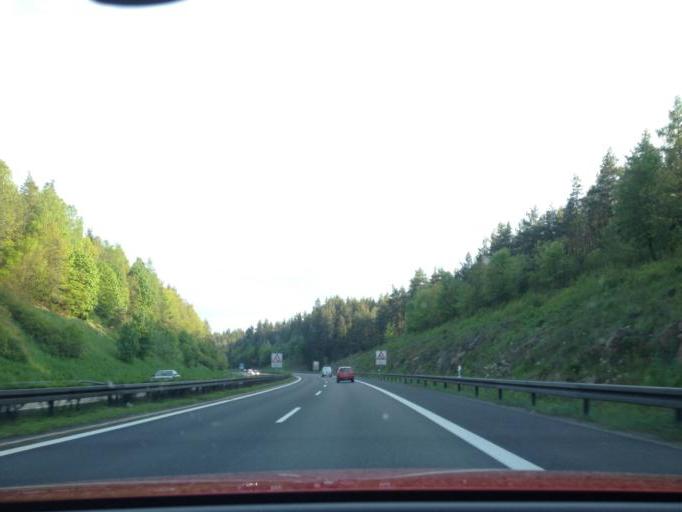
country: DE
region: Bavaria
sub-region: Upper Palatinate
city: Berg
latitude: 49.8260
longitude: 12.1645
